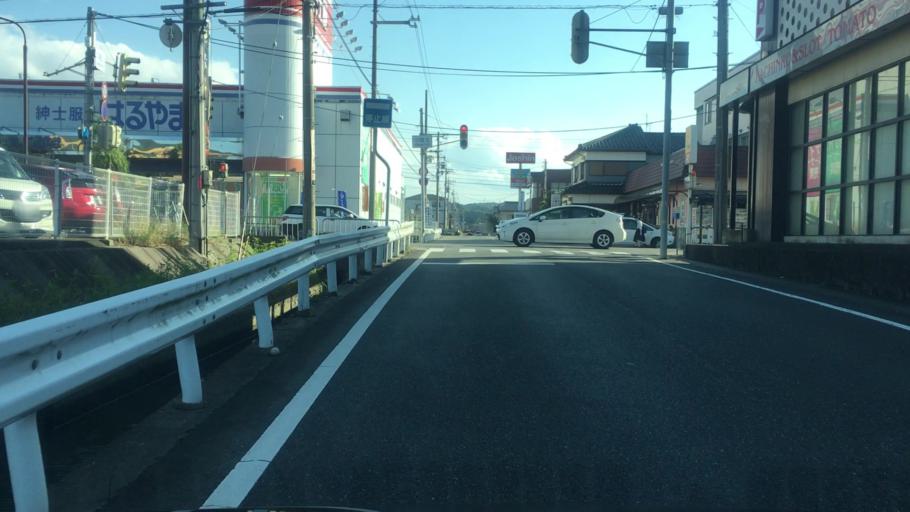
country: JP
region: Hyogo
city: Toyooka
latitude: 35.5545
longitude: 134.8130
